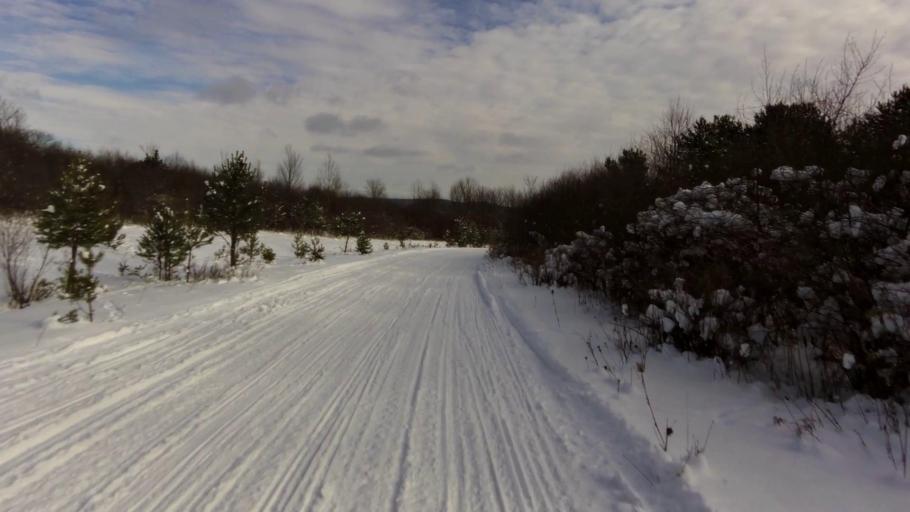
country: US
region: New York
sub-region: Cattaraugus County
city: Franklinville
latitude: 42.3421
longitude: -78.4782
